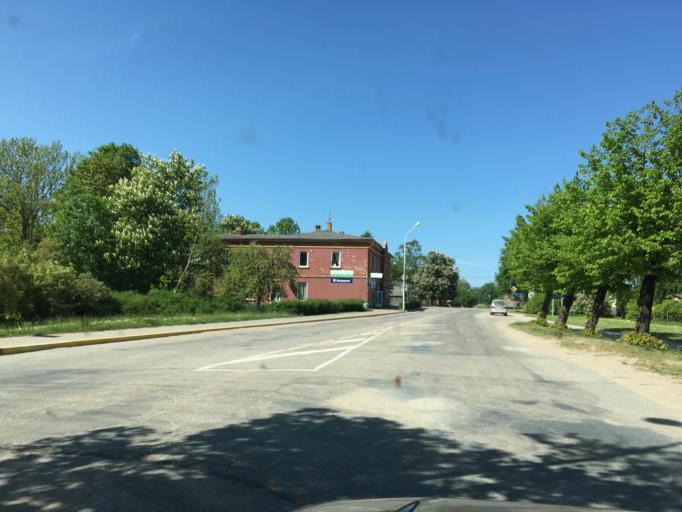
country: LV
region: Dundaga
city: Dundaga
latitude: 57.5081
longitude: 22.3497
